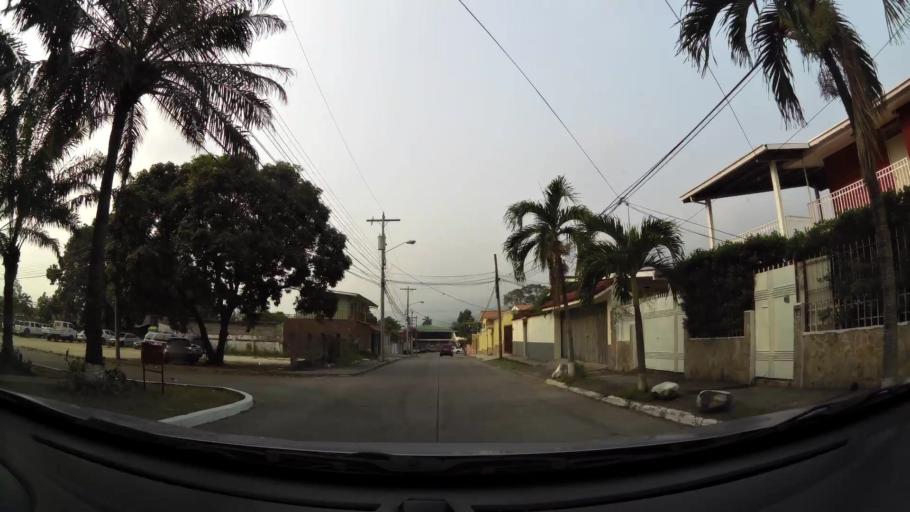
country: HN
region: Cortes
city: Armenta
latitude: 15.4993
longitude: -88.0402
